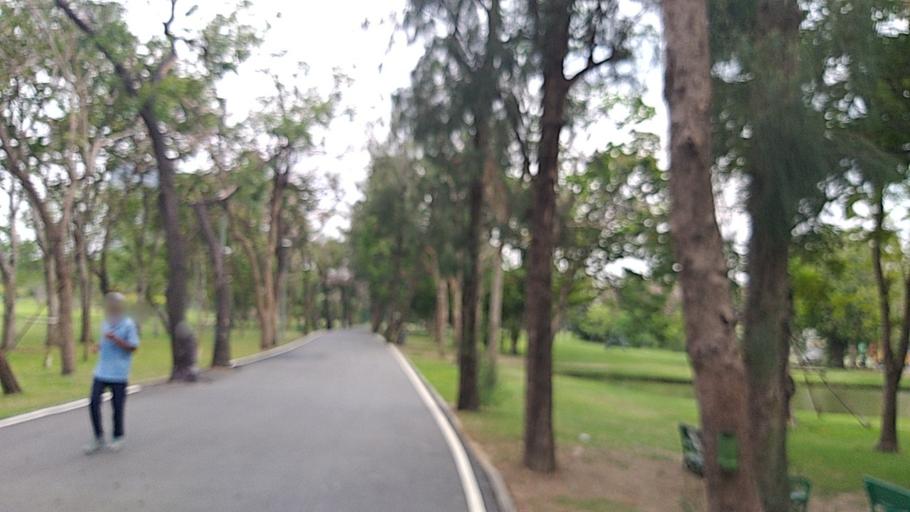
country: TH
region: Bangkok
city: Bang Sue
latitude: 13.8126
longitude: 100.5536
